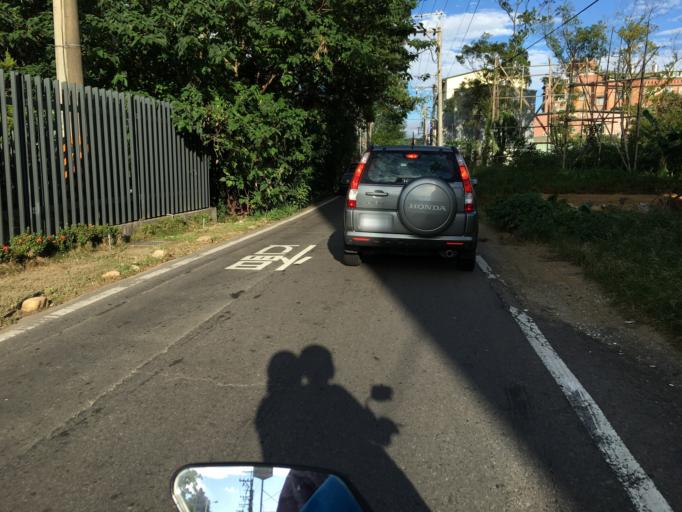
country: TW
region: Taiwan
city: Daxi
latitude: 24.8669
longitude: 121.2232
